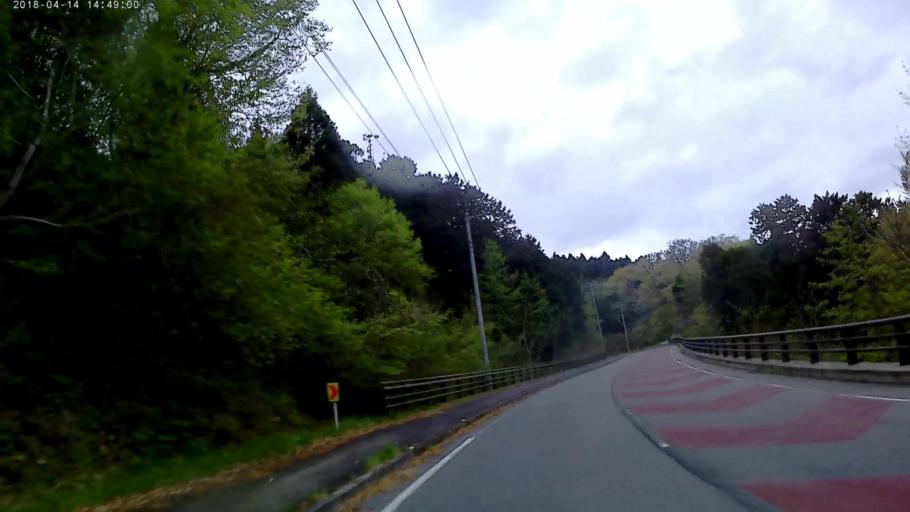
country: JP
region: Shizuoka
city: Gotemba
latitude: 35.3644
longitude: 138.9773
